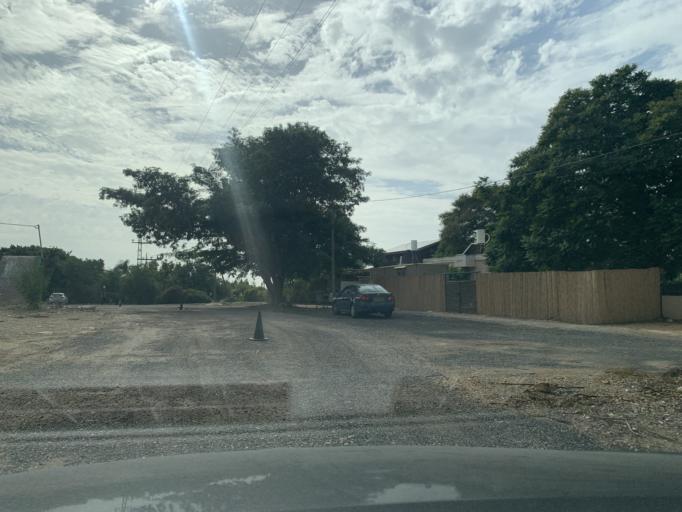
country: IL
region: Central District
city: Et Taiyiba
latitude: 32.2416
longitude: 35.0126
